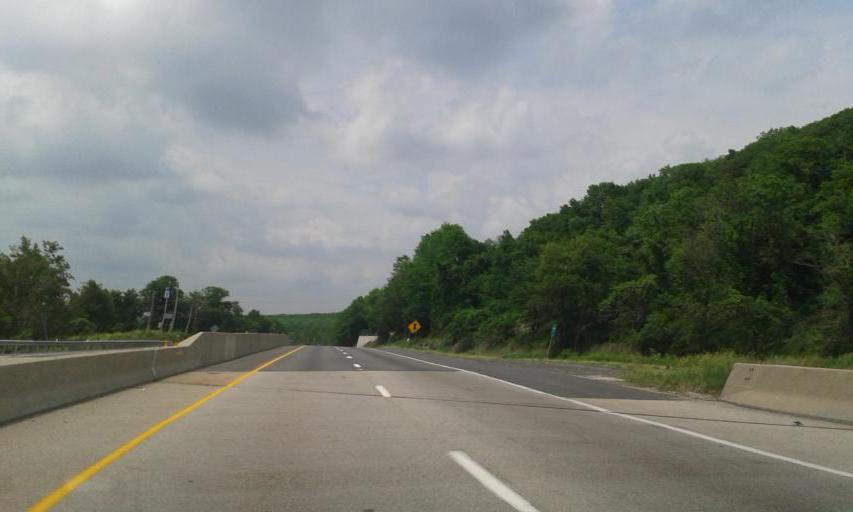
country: US
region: Pennsylvania
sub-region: Northampton County
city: Wind Gap
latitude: 40.8608
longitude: -75.2941
